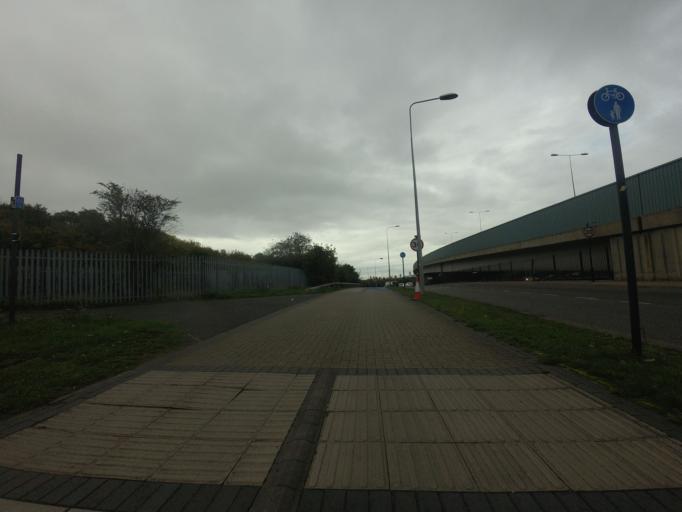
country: GB
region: England
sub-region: Greater London
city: East Ham
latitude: 51.5205
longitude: 0.0611
